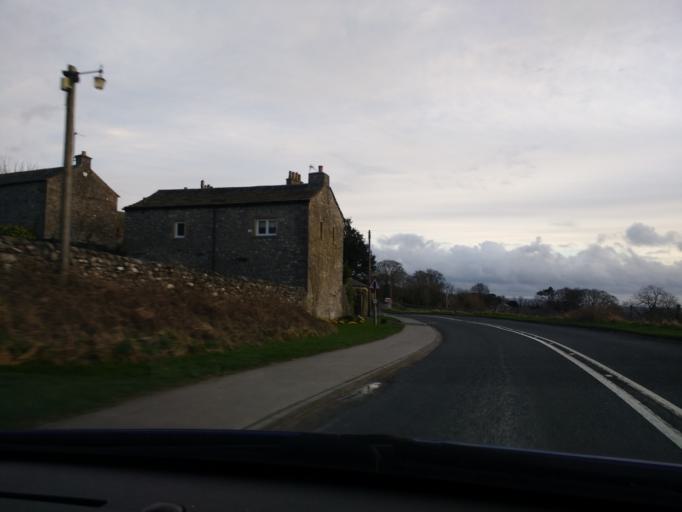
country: GB
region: England
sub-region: North Yorkshire
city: Settle
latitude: 54.0822
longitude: -2.2758
